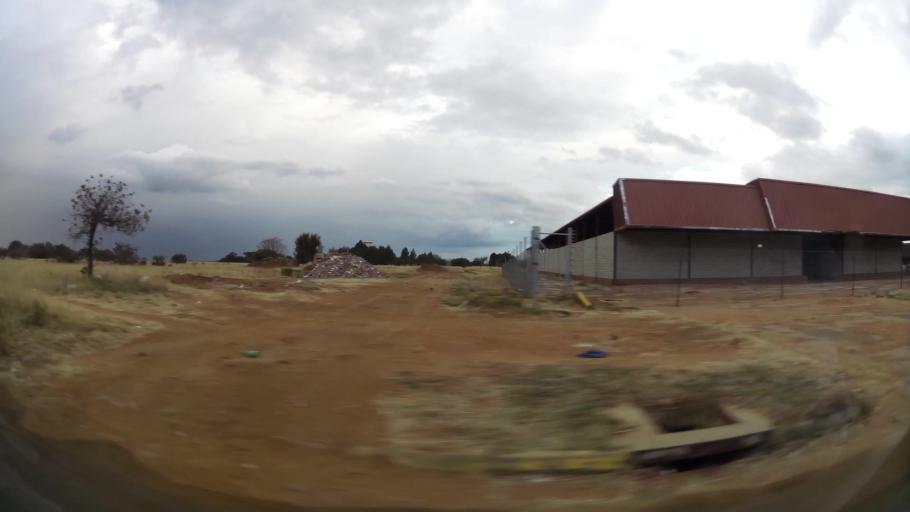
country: ZA
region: Orange Free State
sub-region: Lejweleputswa District Municipality
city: Welkom
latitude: -27.9504
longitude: 26.7351
